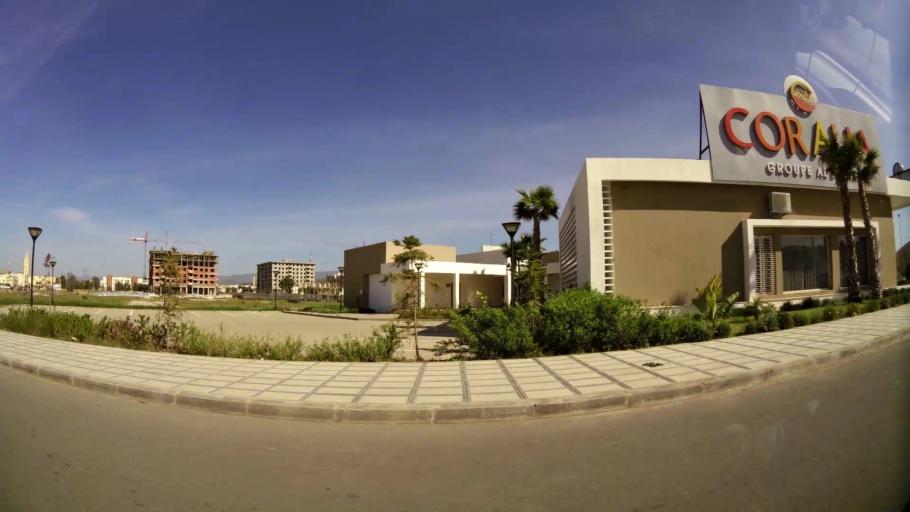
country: MA
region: Oriental
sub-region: Oujda-Angad
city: Oujda
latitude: 34.6649
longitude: -1.9173
